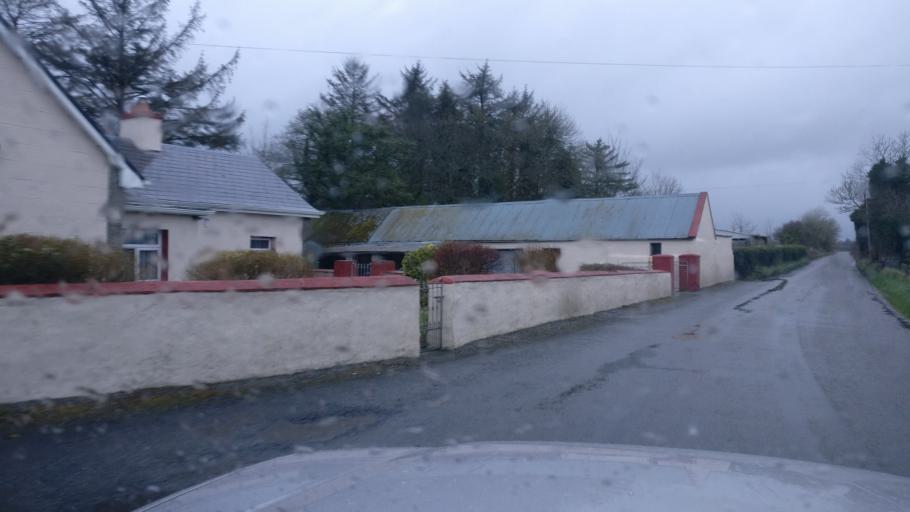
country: IE
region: Connaught
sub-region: County Galway
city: Loughrea
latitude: 53.2560
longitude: -8.4019
